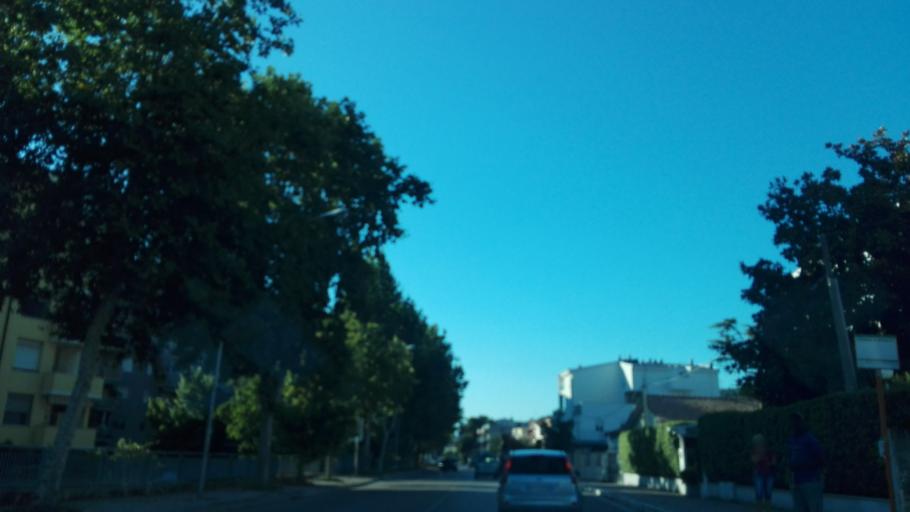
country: IT
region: Abruzzo
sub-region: Provincia di Pescara
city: Villa Raspa
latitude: 42.4917
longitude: 14.1765
